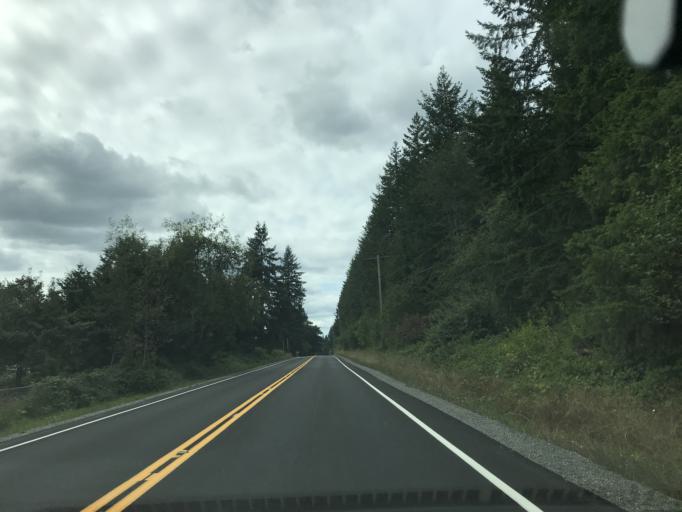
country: US
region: Washington
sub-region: King County
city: Black Diamond
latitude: 47.2867
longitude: -122.0124
